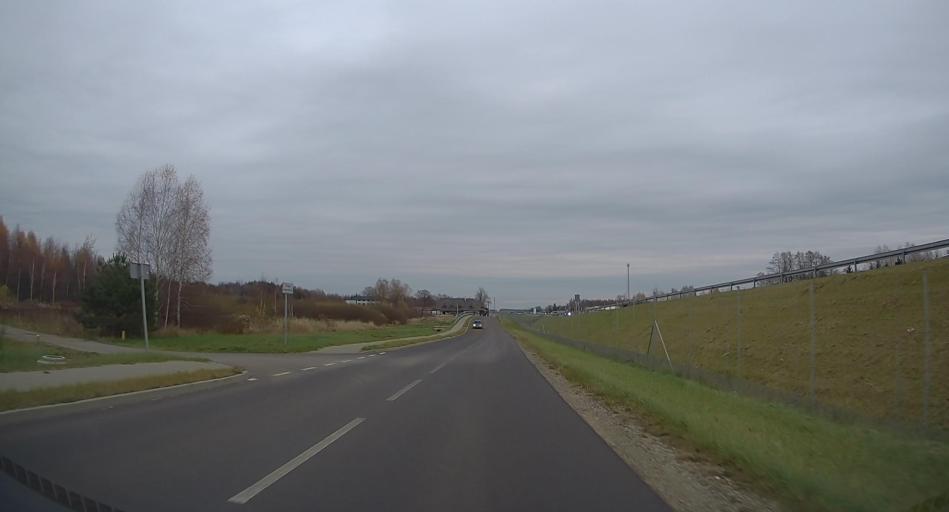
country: PL
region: Lodz Voivodeship
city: Zabia Wola
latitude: 52.0218
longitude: 20.6392
